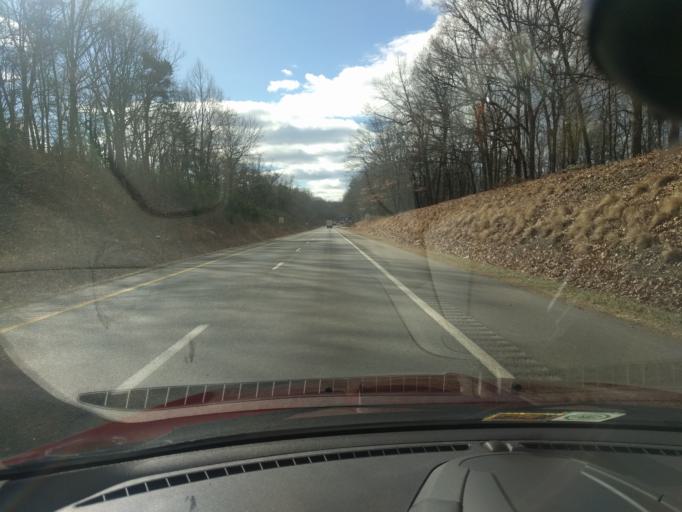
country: US
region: Virginia
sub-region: City of Lynchburg
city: West Lynchburg
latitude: 37.3675
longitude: -79.1569
